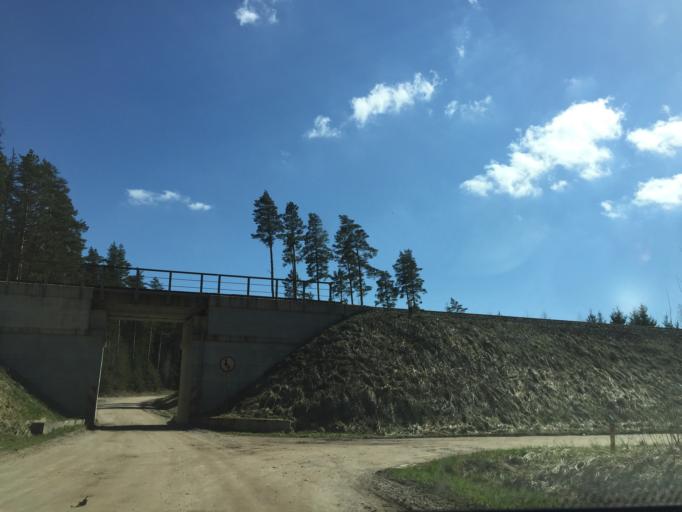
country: EE
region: Valgamaa
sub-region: Valga linn
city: Valga
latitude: 57.8483
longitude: 26.1666
